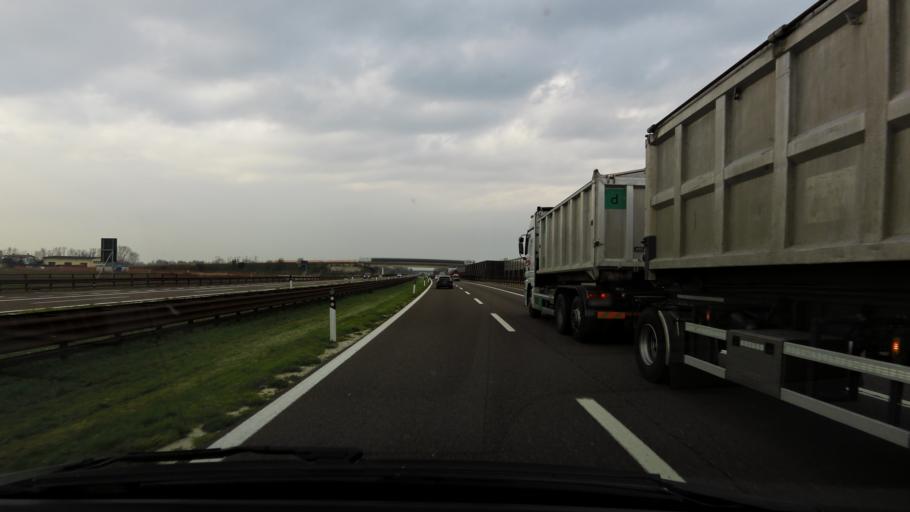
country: IT
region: Veneto
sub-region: Provincia di Verona
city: Vigasio
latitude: 45.3285
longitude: 10.9172
